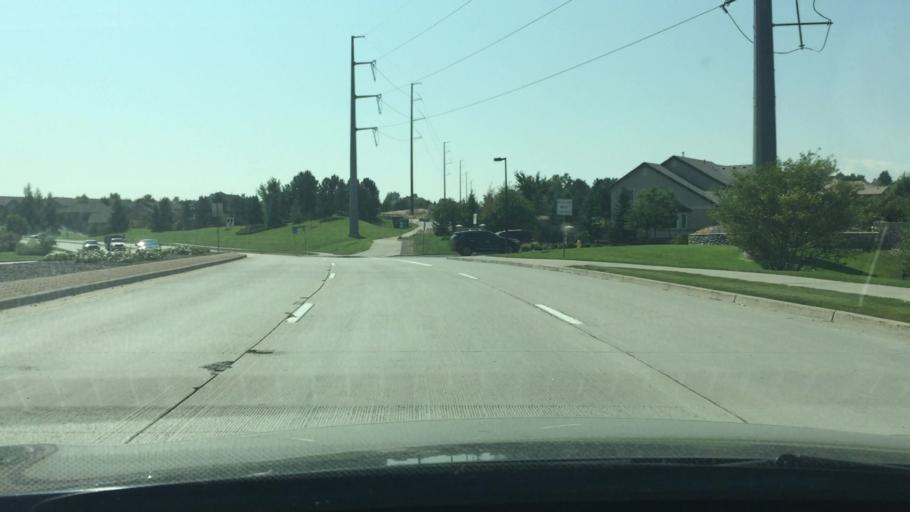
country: US
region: Colorado
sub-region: Arapahoe County
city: Dove Valley
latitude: 39.6092
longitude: -104.7918
